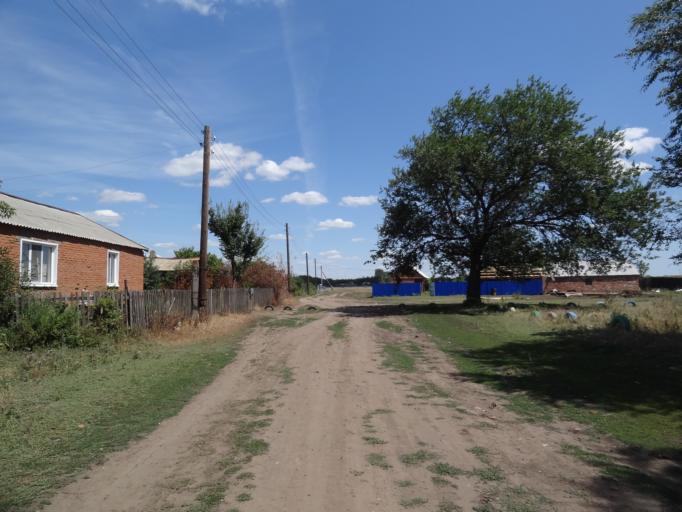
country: RU
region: Saratov
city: Sovetskoye
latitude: 51.2840
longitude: 46.6483
